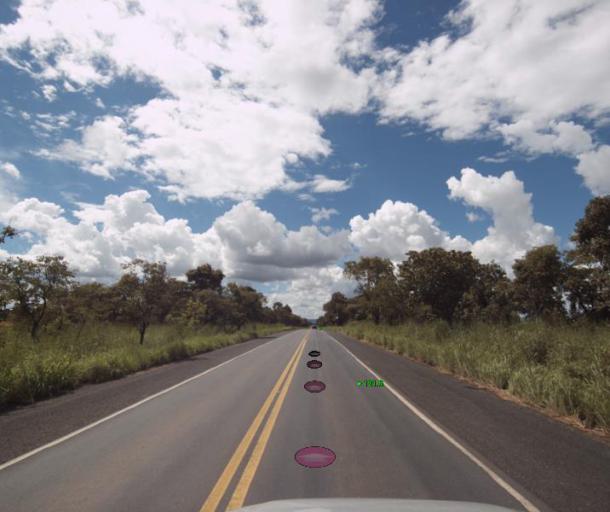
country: BR
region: Goias
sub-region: Porangatu
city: Porangatu
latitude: -13.8420
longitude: -49.0461
